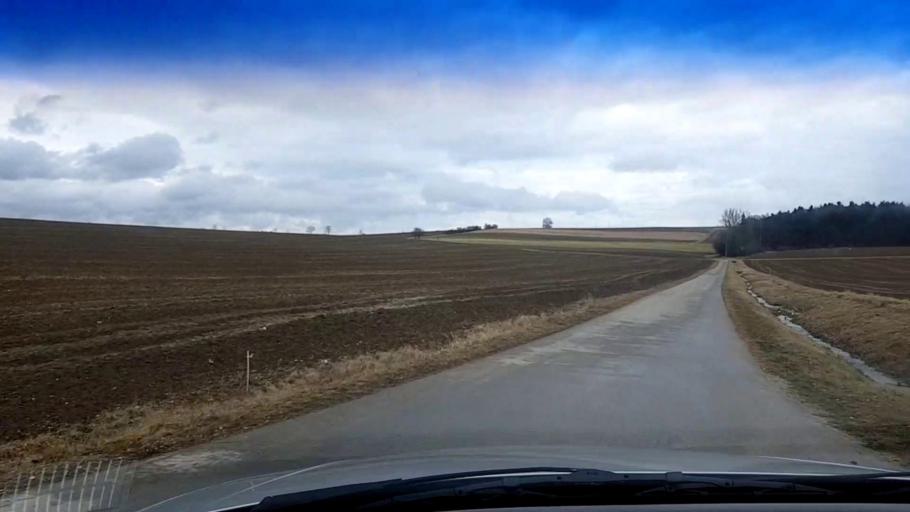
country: DE
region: Bavaria
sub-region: Upper Franconia
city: Zapfendorf
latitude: 50.0084
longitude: 10.9770
